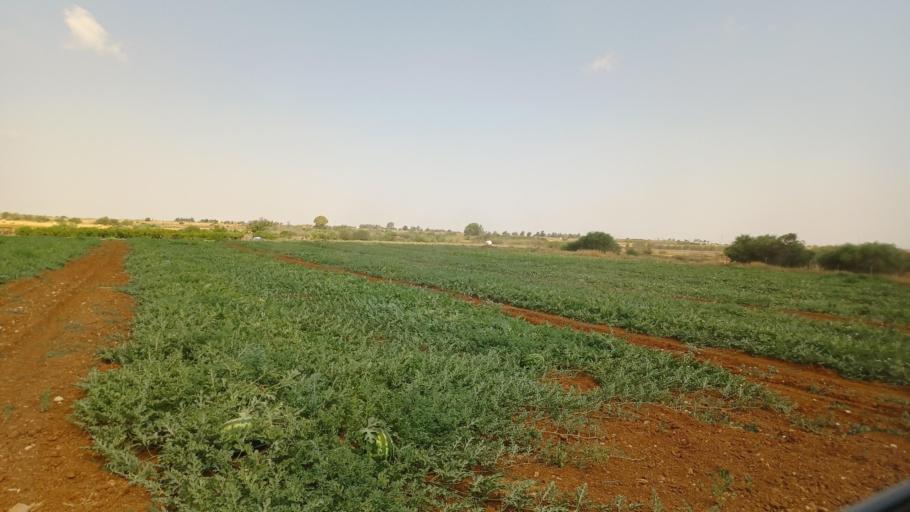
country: CY
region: Ammochostos
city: Frenaros
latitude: 35.0610
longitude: 33.9215
